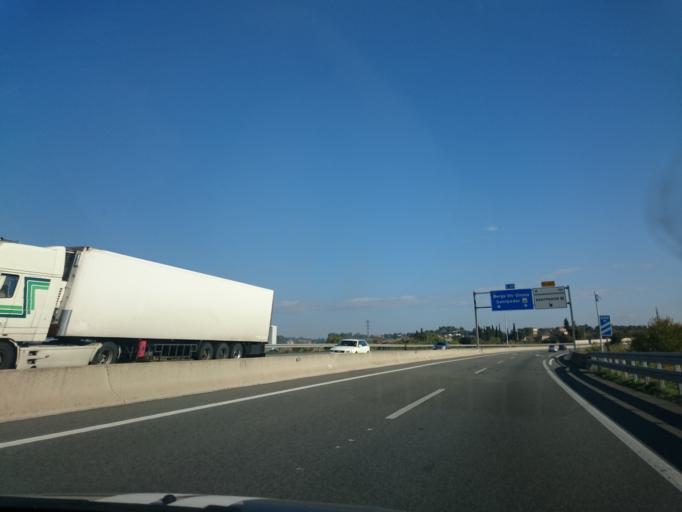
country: ES
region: Catalonia
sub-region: Provincia de Barcelona
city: Manresa
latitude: 41.7477
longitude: 1.8339
